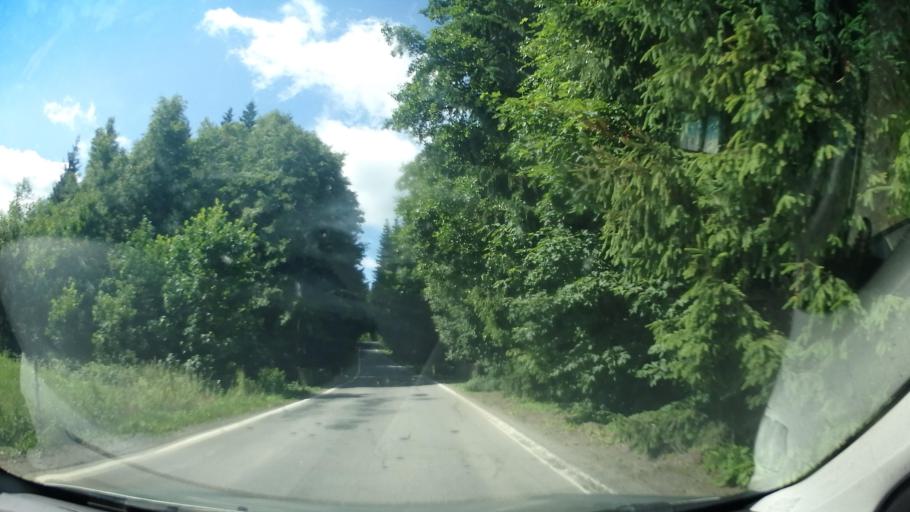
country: CZ
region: Vysocina
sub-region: Okres Zd'ar nad Sazavou
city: Nove Mesto na Morave
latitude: 49.6296
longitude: 16.0745
